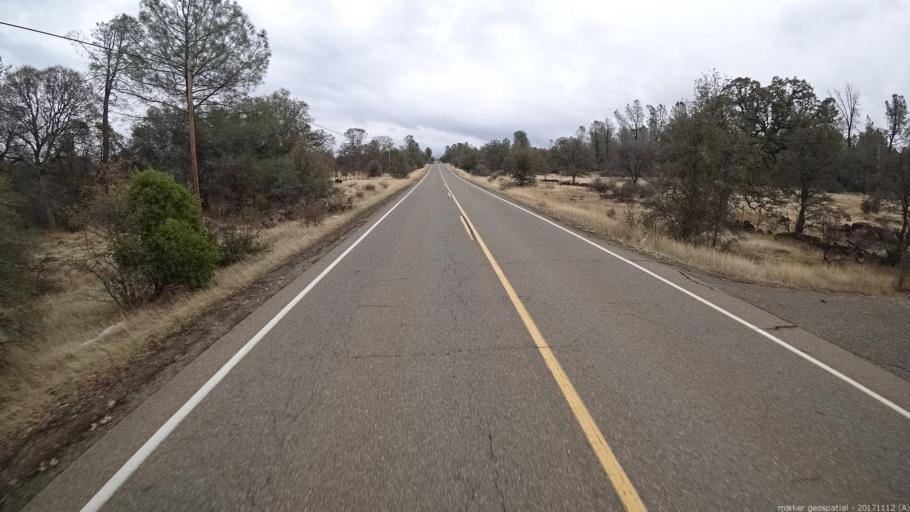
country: US
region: California
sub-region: Shasta County
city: Palo Cedro
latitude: 40.4812
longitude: -122.0965
